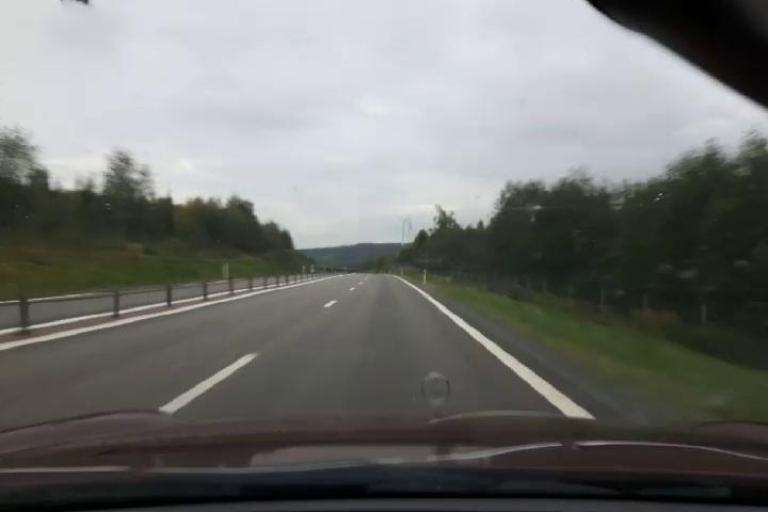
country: SE
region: Vaesternorrland
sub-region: Haernoesands Kommun
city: Haernoesand
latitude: 62.7616
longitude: 17.9054
